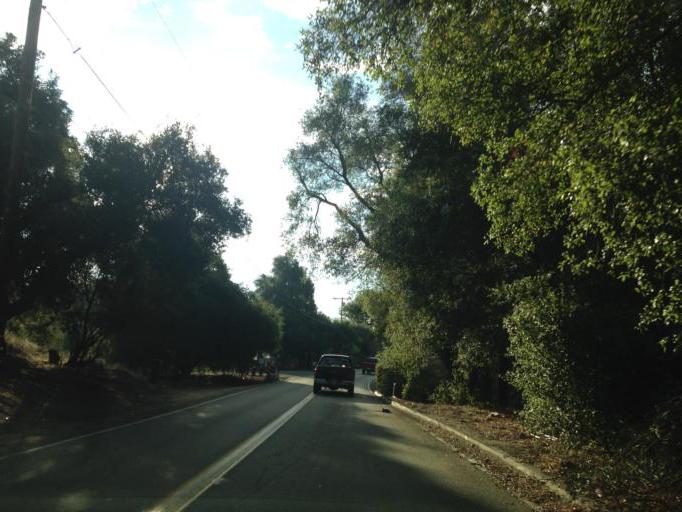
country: US
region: California
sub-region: San Diego County
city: Rainbow
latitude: 33.4397
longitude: -117.0911
